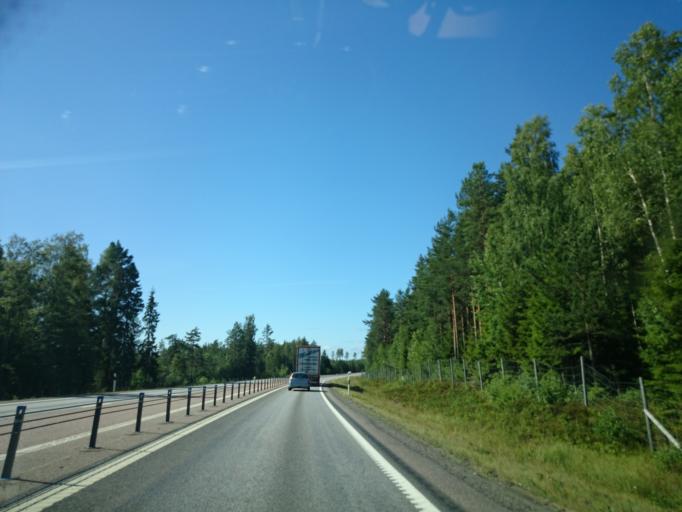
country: SE
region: Gaevleborg
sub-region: Soderhamns Kommun
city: Ljusne
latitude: 61.1132
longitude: 17.0115
